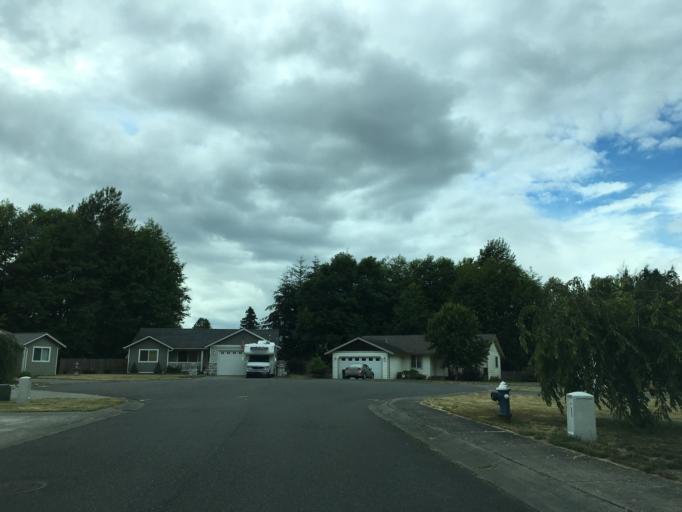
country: US
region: Washington
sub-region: Whatcom County
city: Birch Bay
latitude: 48.9500
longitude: -122.7440
